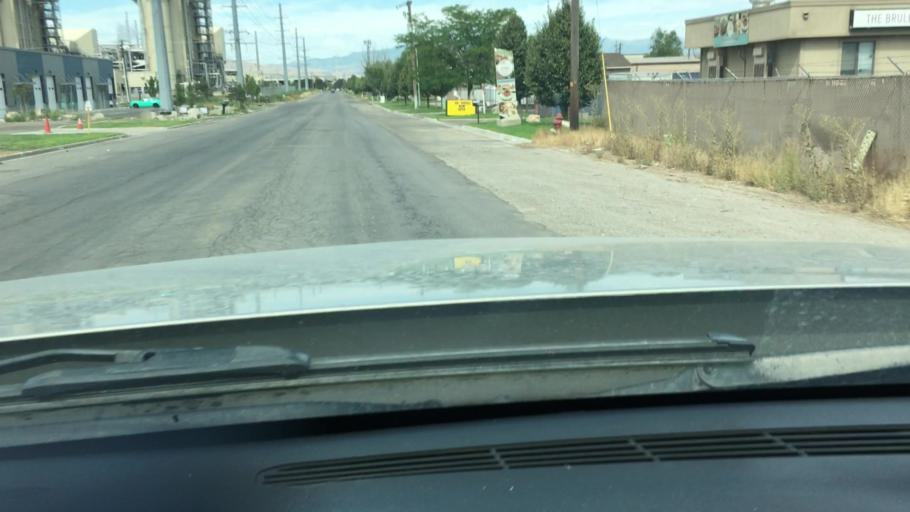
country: US
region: Utah
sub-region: Utah County
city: Lindon
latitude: 40.3335
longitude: -111.7516
